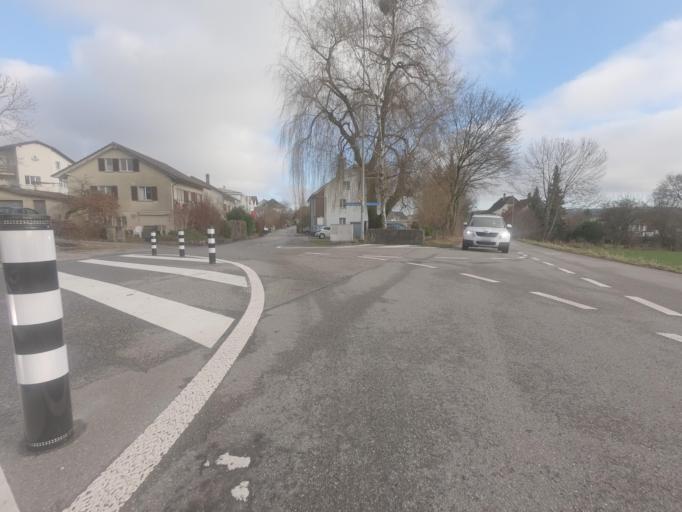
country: CH
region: Solothurn
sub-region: Bezirk Lebern
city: Langendorf
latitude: 47.2121
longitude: 7.4890
